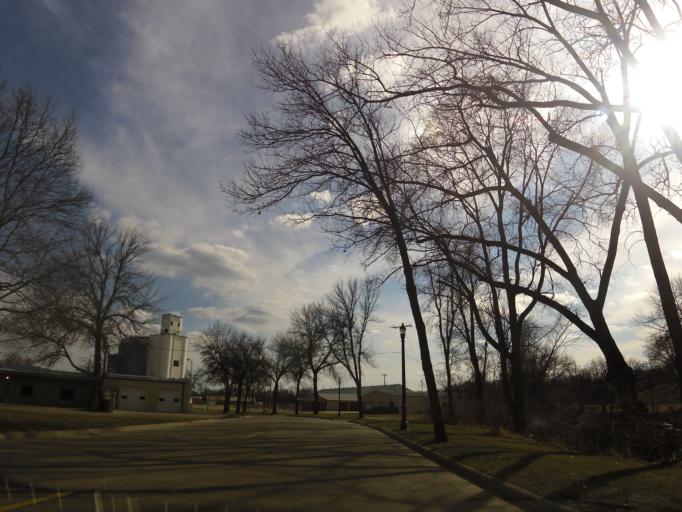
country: US
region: Minnesota
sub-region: Chippewa County
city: Montevideo
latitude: 44.9451
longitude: -95.7259
